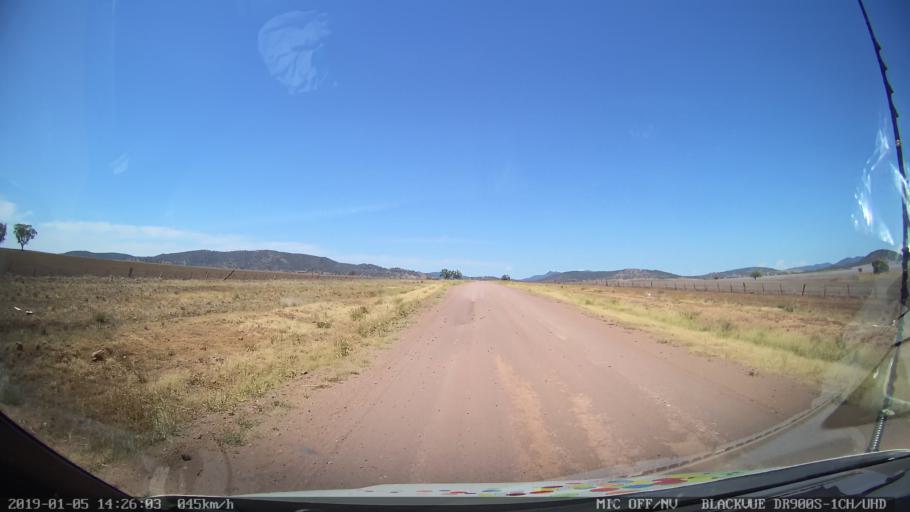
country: AU
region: New South Wales
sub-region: Liverpool Plains
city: Quirindi
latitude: -31.2388
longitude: 150.5542
